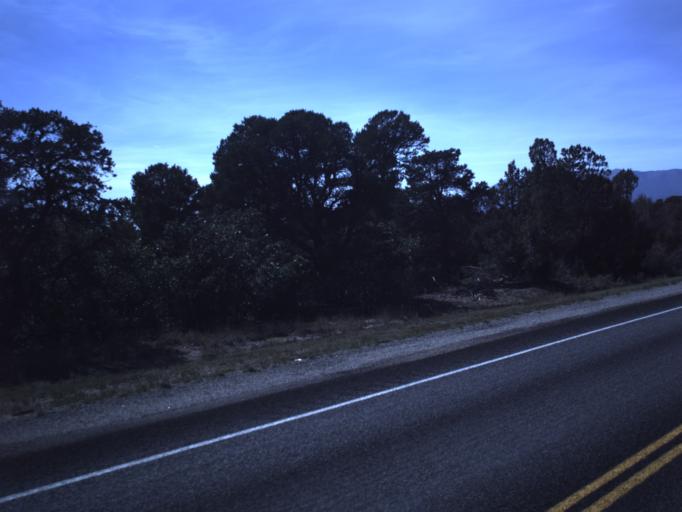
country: US
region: Utah
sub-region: San Juan County
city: Monticello
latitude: 37.8414
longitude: -109.1287
